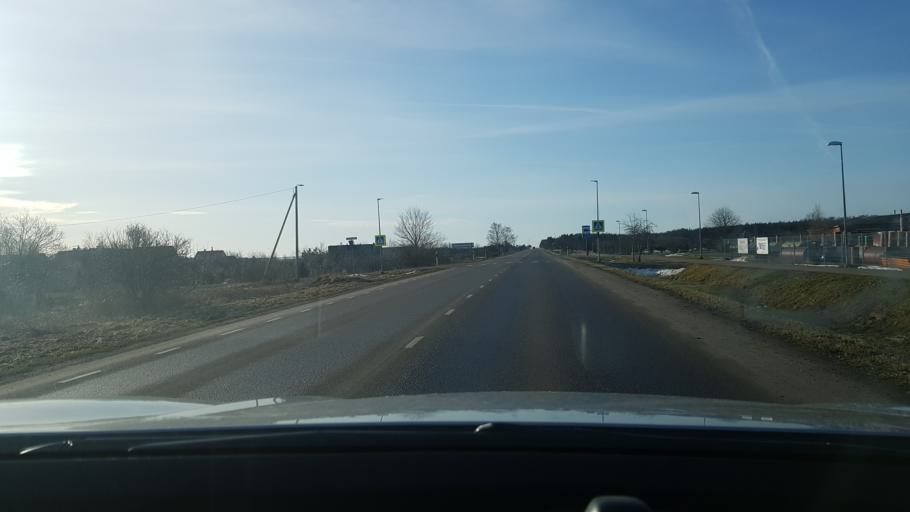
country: EE
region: Saare
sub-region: Kuressaare linn
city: Kuressaare
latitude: 58.2520
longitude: 22.5086
